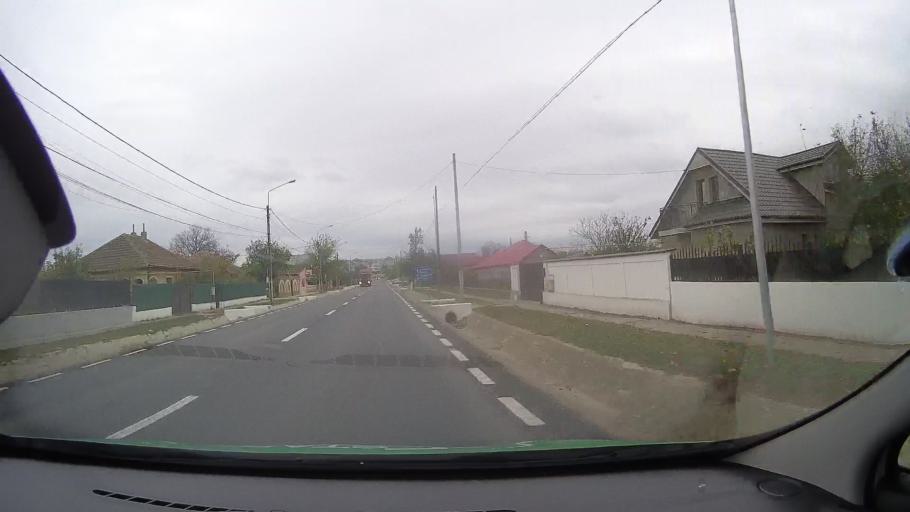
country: RO
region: Constanta
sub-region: Comuna Mihail Kogalniceanu
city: Mihail Kogalniceanu
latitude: 44.3674
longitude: 28.4572
